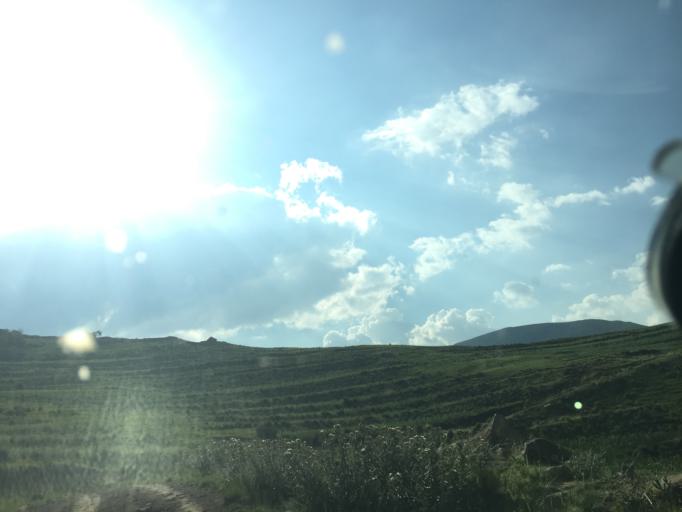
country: LS
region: Maseru
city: Nako
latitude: -29.6278
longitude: 28.1062
